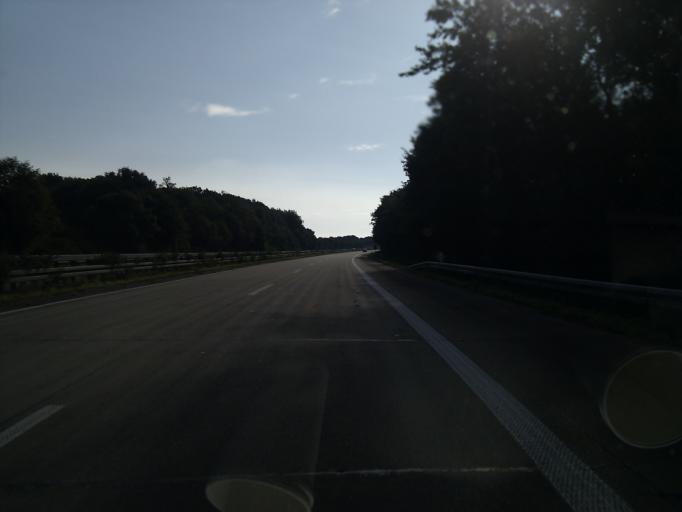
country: DE
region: North Rhine-Westphalia
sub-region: Regierungsbezirk Dusseldorf
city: Goch
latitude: 51.6746
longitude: 6.0999
